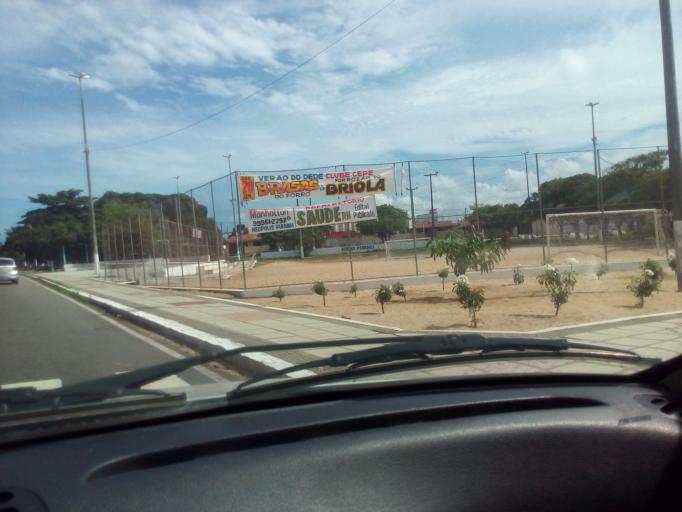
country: BR
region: Rio Grande do Norte
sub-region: Natal
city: Natal
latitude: -5.8680
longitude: -35.2017
